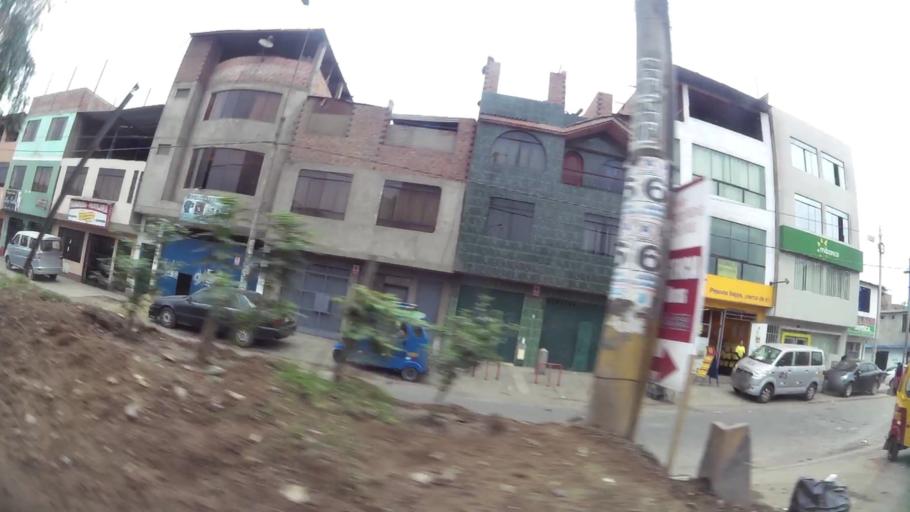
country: PE
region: Lima
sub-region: Lima
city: Surco
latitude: -12.1781
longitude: -76.9626
